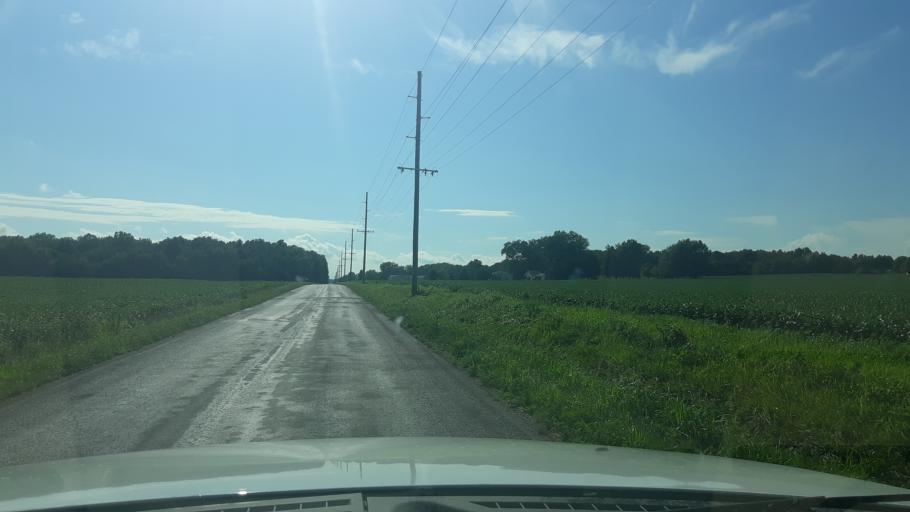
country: US
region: Illinois
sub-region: Saline County
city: Harrisburg
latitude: 37.8630
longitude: -88.5548
